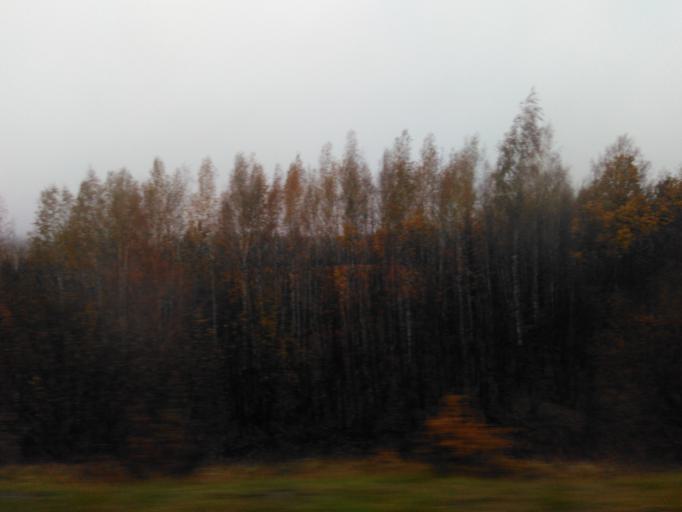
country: RU
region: Tatarstan
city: Sviyazhsk
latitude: 55.7293
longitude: 48.7660
